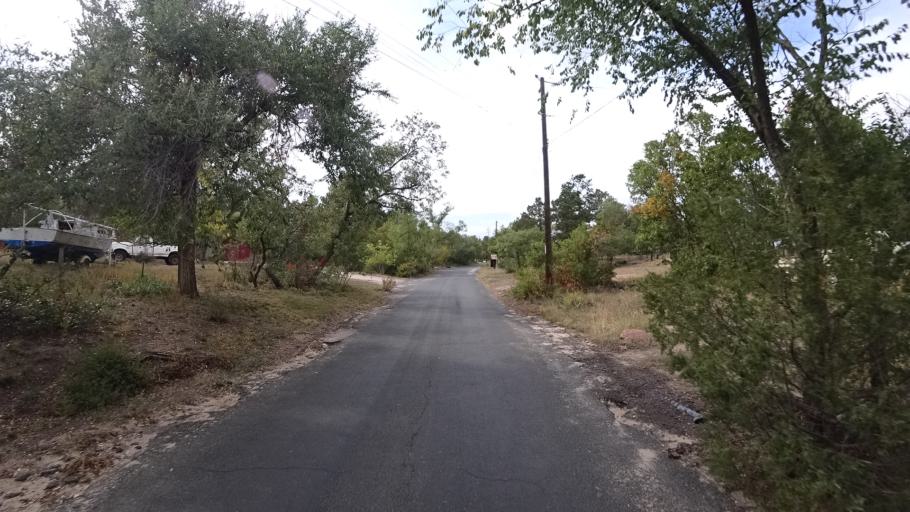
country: US
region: Colorado
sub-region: El Paso County
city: Cimarron Hills
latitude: 38.8745
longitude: -104.7597
